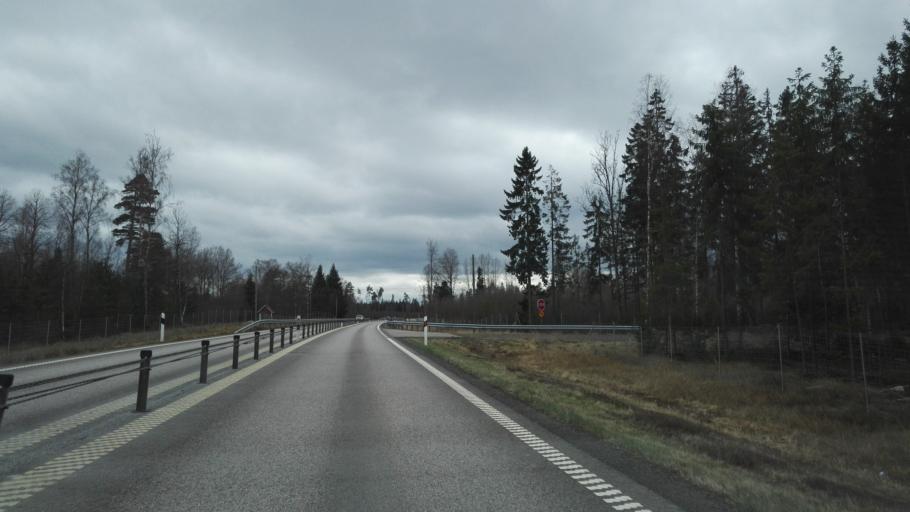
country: SE
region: Kronoberg
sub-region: Alvesta Kommun
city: Vislanda
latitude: 56.6768
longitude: 14.3150
